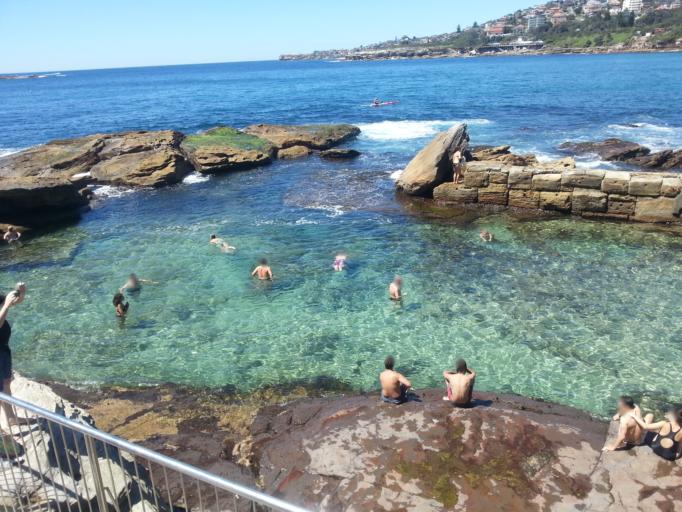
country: AU
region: New South Wales
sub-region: Randwick
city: Coogee
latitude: -33.9200
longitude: 151.2606
